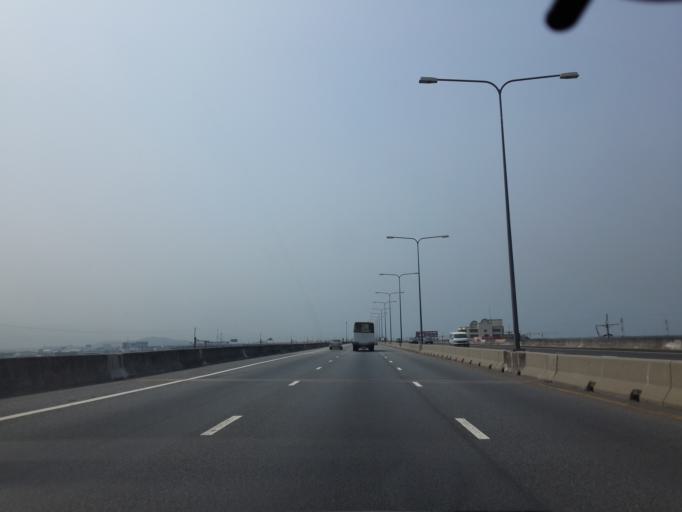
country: TH
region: Chachoengsao
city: Bang Pakong
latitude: 13.4717
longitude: 100.9984
